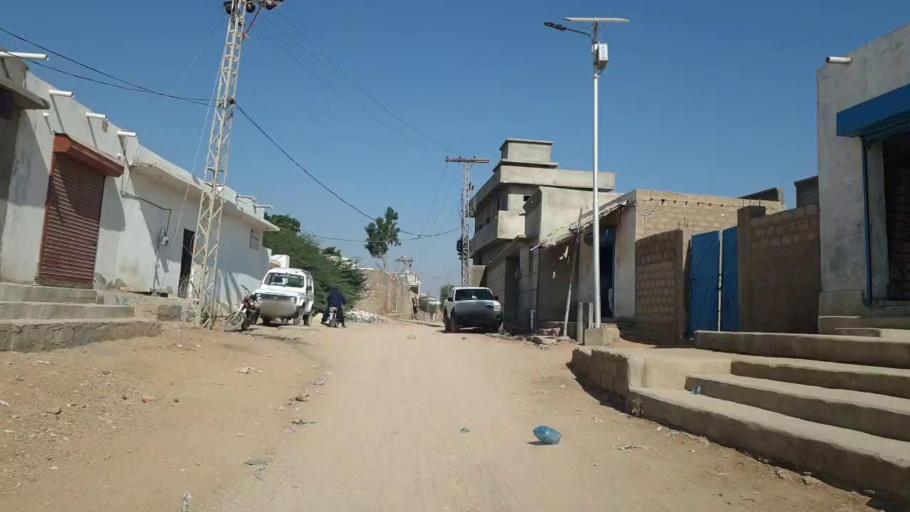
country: PK
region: Sindh
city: Jamshoro
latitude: 25.3575
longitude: 67.8321
